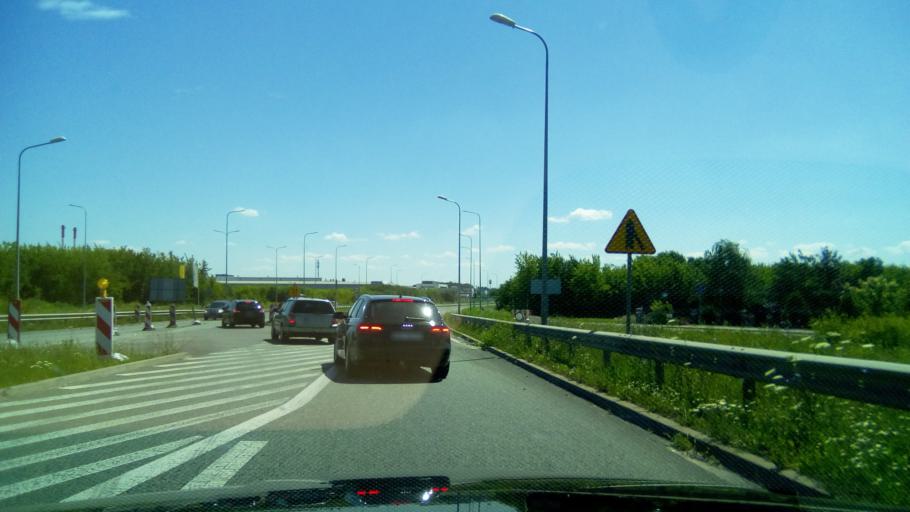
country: PL
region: Masovian Voivodeship
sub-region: Radom
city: Radom
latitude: 51.4189
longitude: 21.1892
